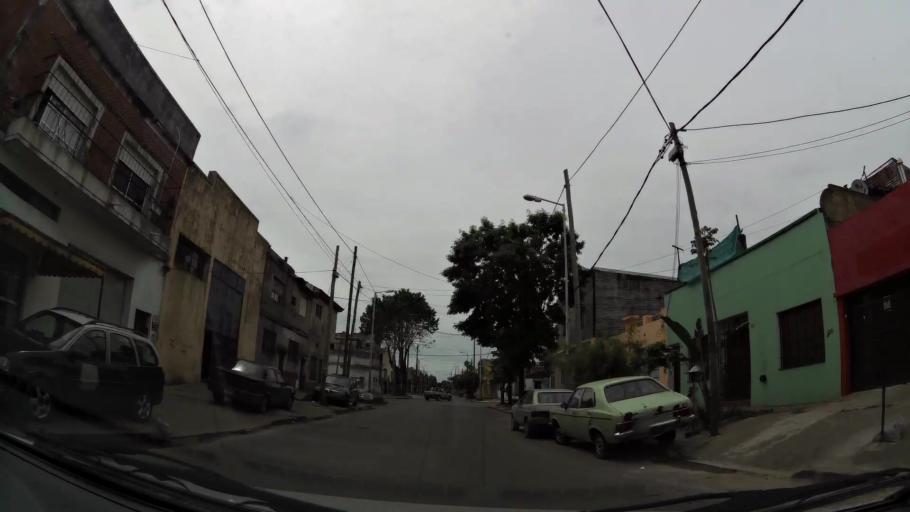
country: AR
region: Buenos Aires
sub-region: Partido de Avellaneda
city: Avellaneda
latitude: -34.6541
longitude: -58.3499
